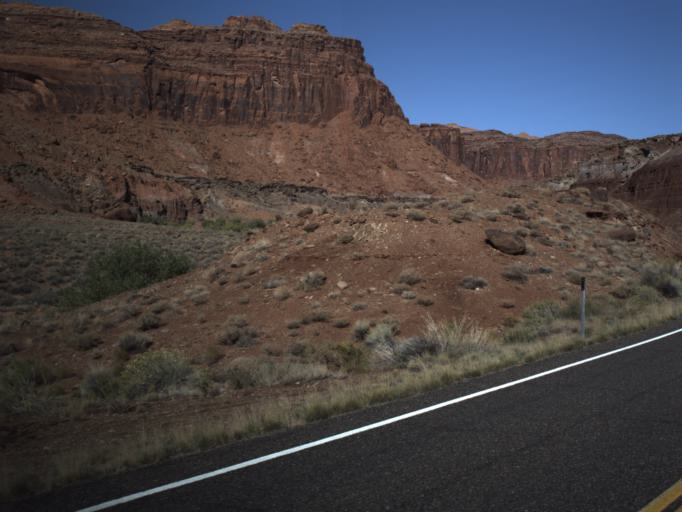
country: US
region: Utah
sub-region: San Juan County
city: Blanding
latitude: 37.9030
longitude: -110.4503
